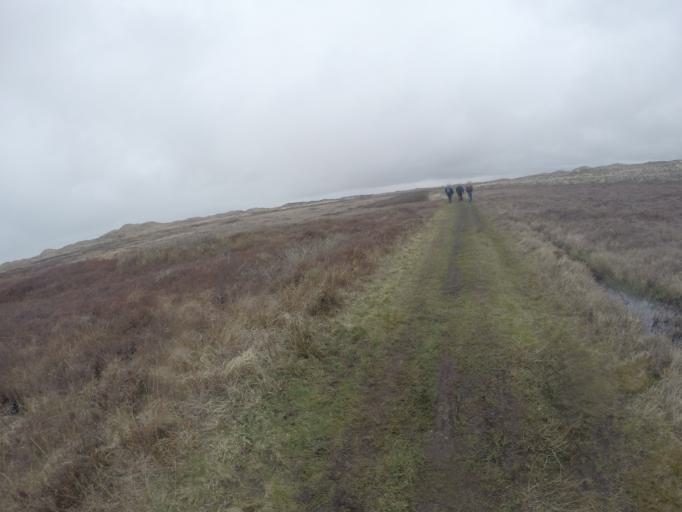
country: DK
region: Central Jutland
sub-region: Lemvig Kommune
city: Thyboron
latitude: 56.8357
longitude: 8.2719
